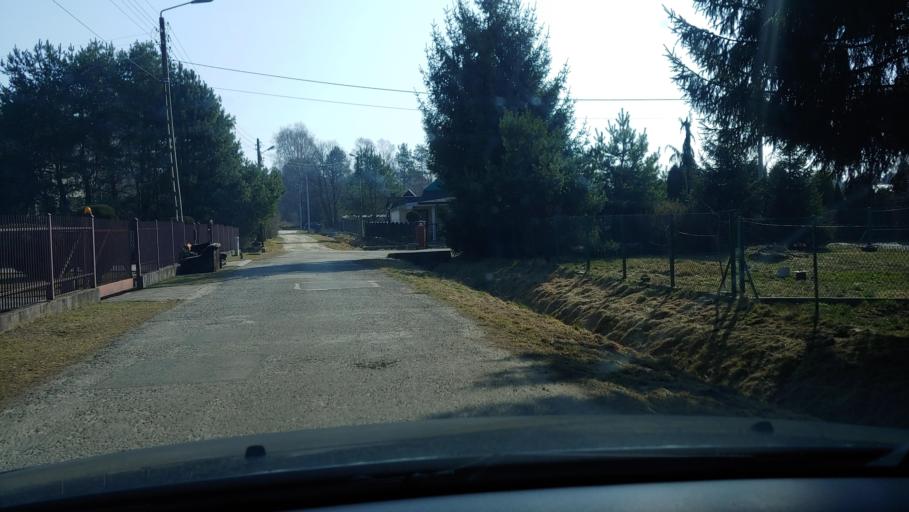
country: PL
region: Lesser Poland Voivodeship
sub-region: Powiat chrzanowski
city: Luszowice
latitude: 50.1540
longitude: 19.4320
